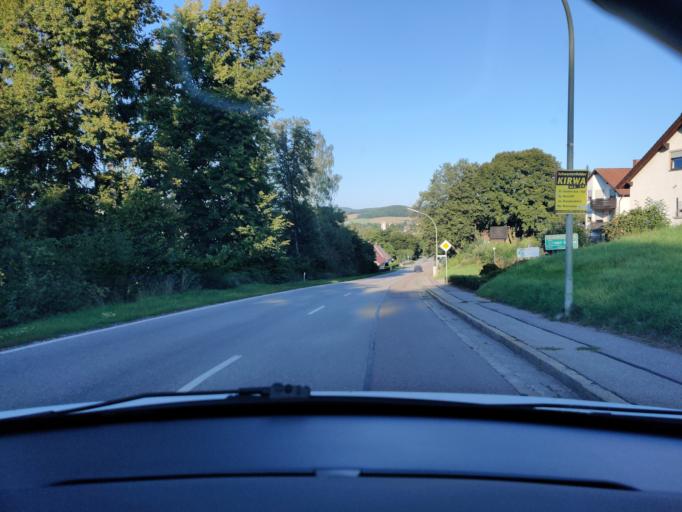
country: DE
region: Bavaria
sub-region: Upper Palatinate
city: Nabburg
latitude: 49.4470
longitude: 12.1686
